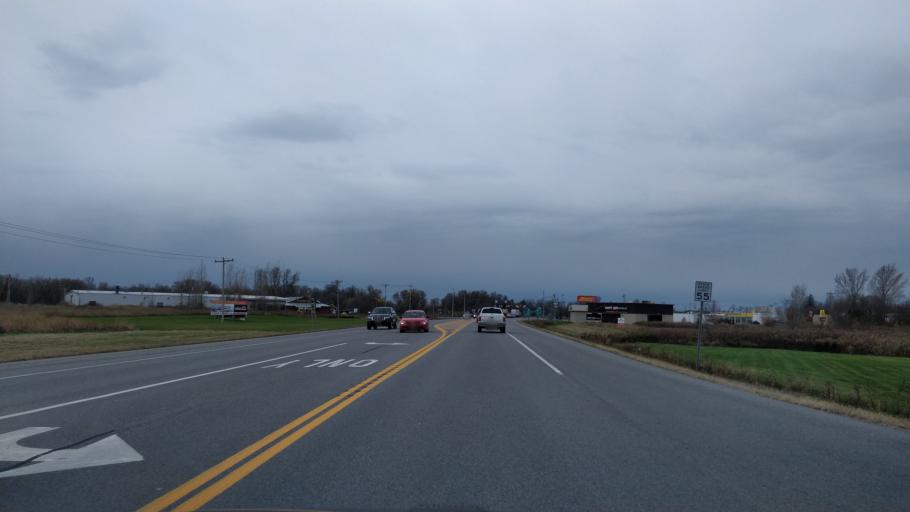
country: US
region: New York
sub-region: St. Lawrence County
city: Ogdensburg
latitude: 44.6923
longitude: -75.4721
